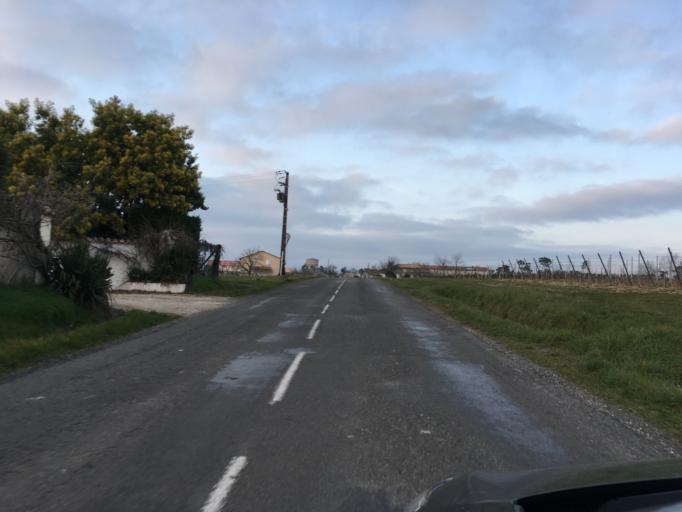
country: FR
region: Aquitaine
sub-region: Departement de la Gironde
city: Saint-Ciers-sur-Gironde
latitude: 45.3107
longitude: -0.5961
